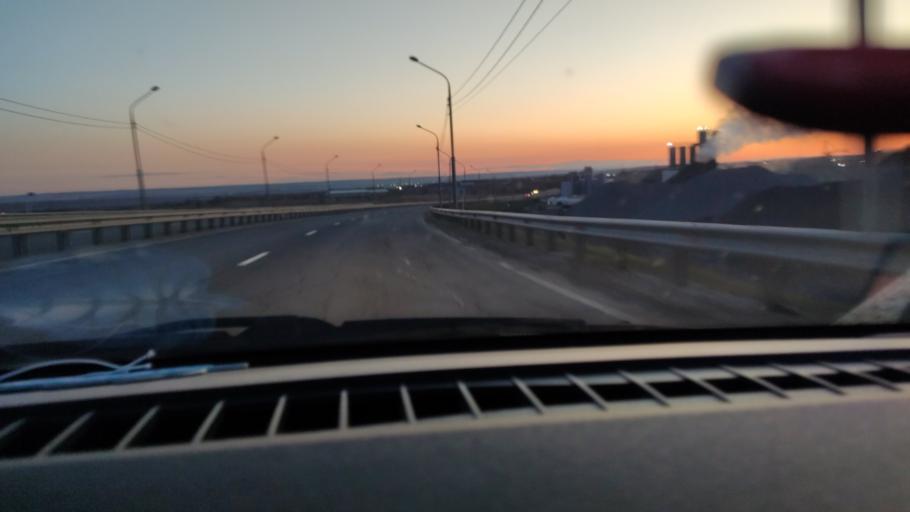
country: RU
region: Saratov
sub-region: Saratovskiy Rayon
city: Saratov
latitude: 51.6447
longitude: 45.9862
